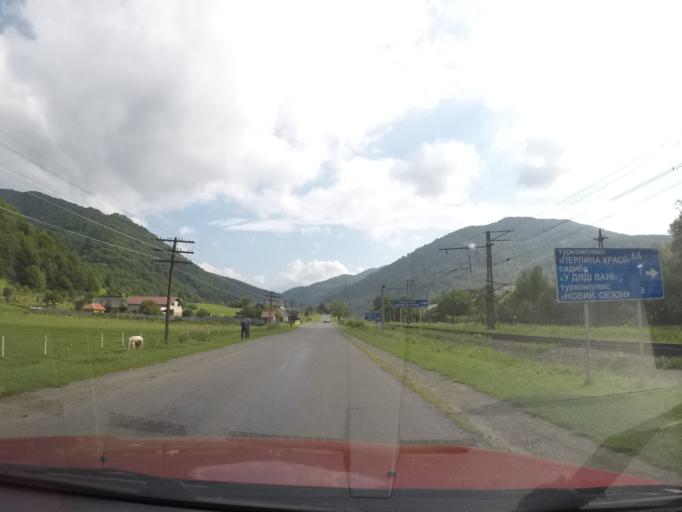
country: UA
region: Zakarpattia
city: Velykyi Bereznyi
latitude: 48.9496
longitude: 22.6058
